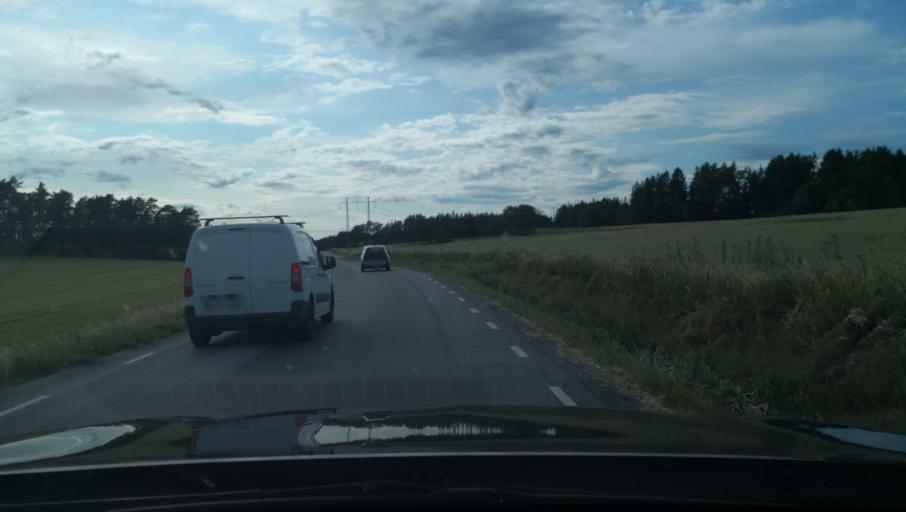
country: SE
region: Uppsala
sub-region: Enkopings Kommun
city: Orsundsbro
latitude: 59.6741
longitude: 17.4303
